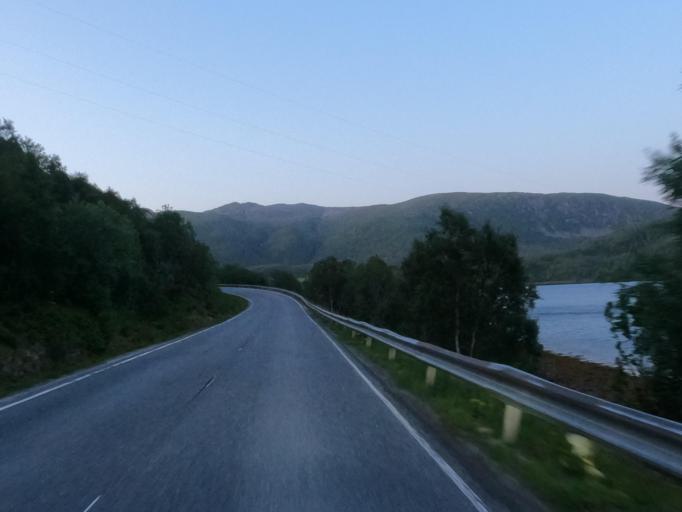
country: NO
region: Nordland
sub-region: Lodingen
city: Lodingen
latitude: 68.5629
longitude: 15.7926
